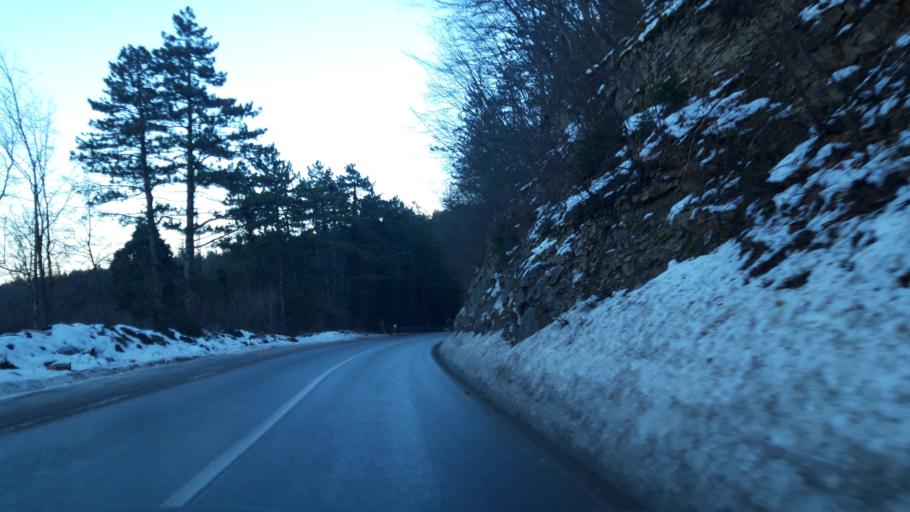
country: BA
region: Republika Srpska
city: Vlasenica
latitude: 44.1729
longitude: 18.9471
